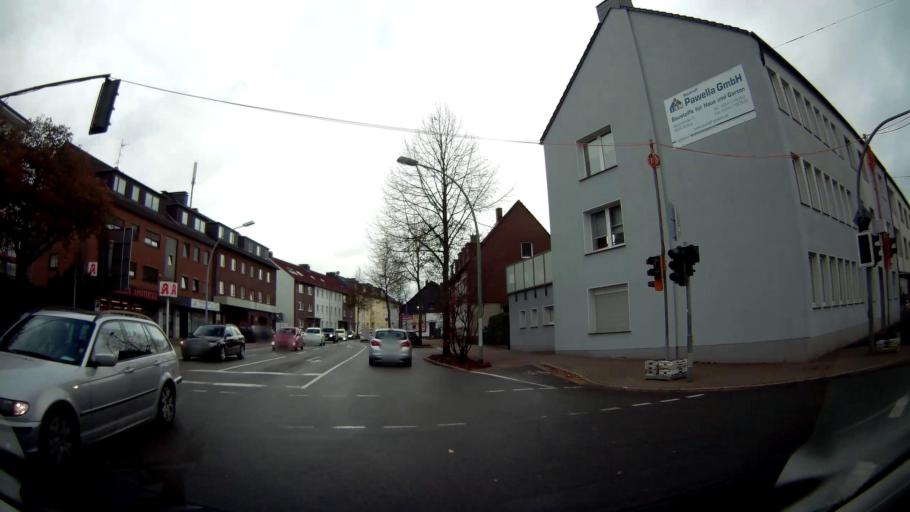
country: DE
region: North Rhine-Westphalia
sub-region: Regierungsbezirk Munster
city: Bottrop
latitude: 51.5296
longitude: 6.9414
